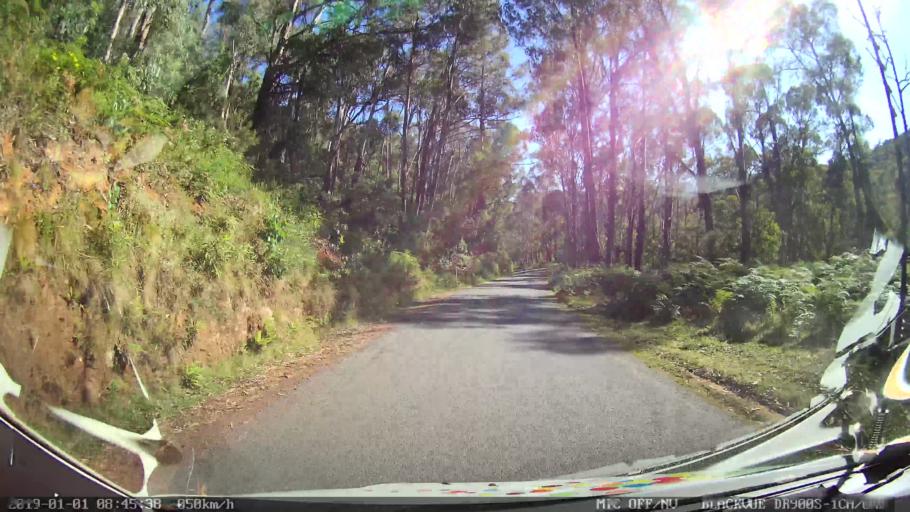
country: AU
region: New South Wales
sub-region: Snowy River
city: Jindabyne
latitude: -36.3044
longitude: 148.1894
